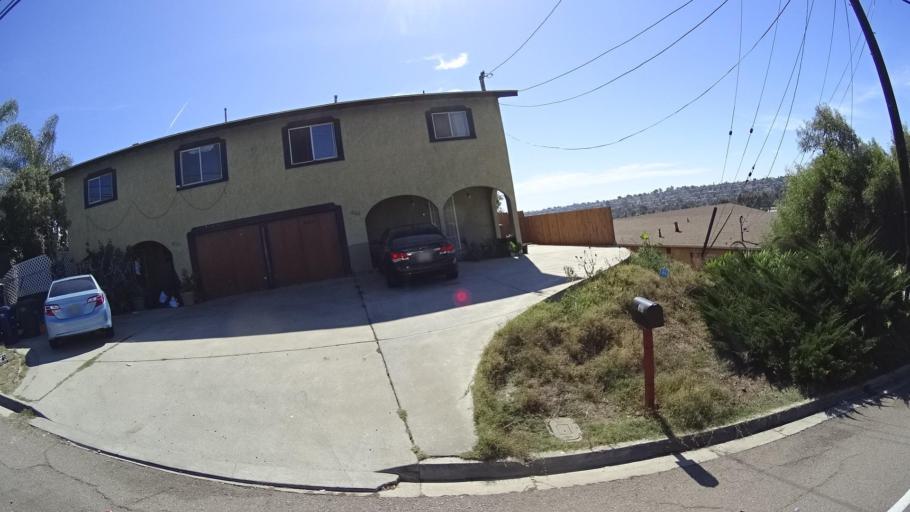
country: US
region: California
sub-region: San Diego County
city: La Presa
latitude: 32.7190
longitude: -117.0108
